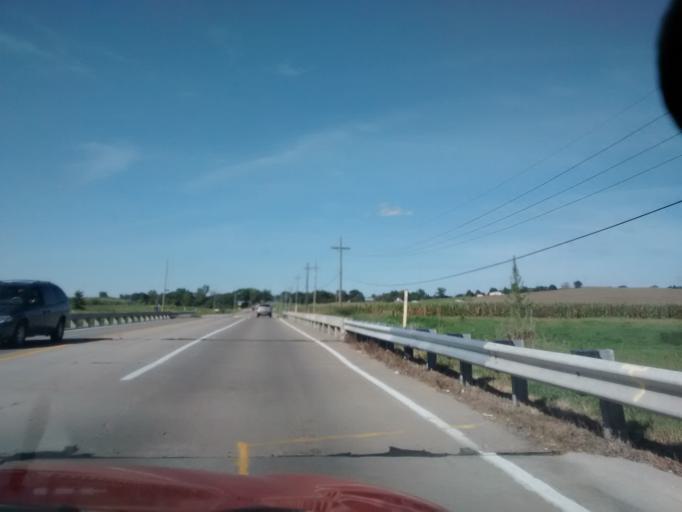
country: US
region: Nebraska
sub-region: Sarpy County
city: Offutt Air Force Base
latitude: 41.1438
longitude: -95.9667
